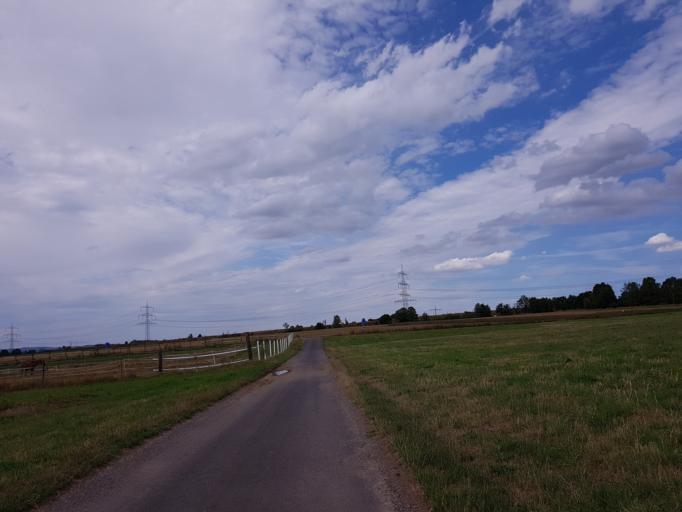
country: DE
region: Hesse
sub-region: Regierungsbezirk Giessen
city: Langgons
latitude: 50.5144
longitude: 8.6620
